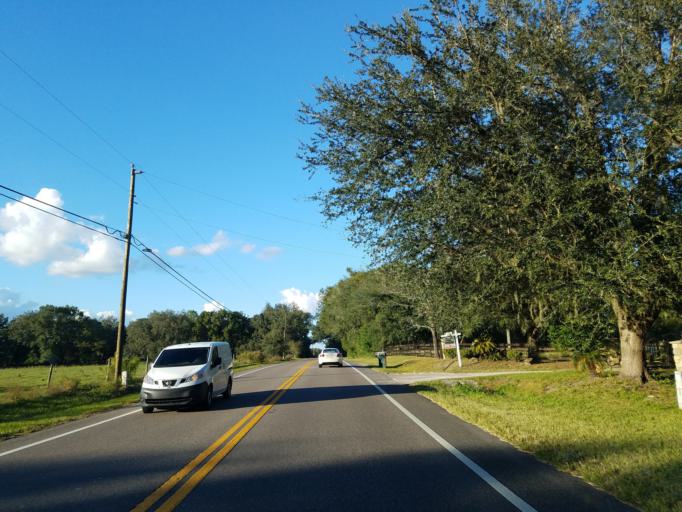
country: US
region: Florida
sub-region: Hernando County
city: Hill 'n Dale
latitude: 28.5027
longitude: -82.3030
